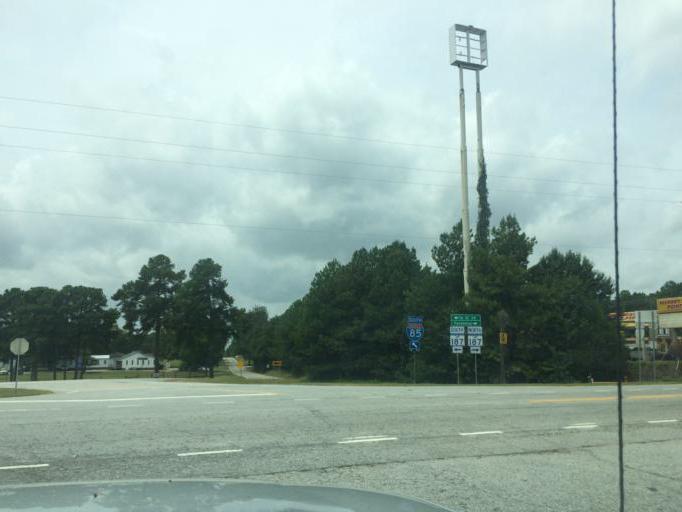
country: US
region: South Carolina
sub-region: Anderson County
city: Centerville
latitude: 34.5479
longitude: -82.8075
